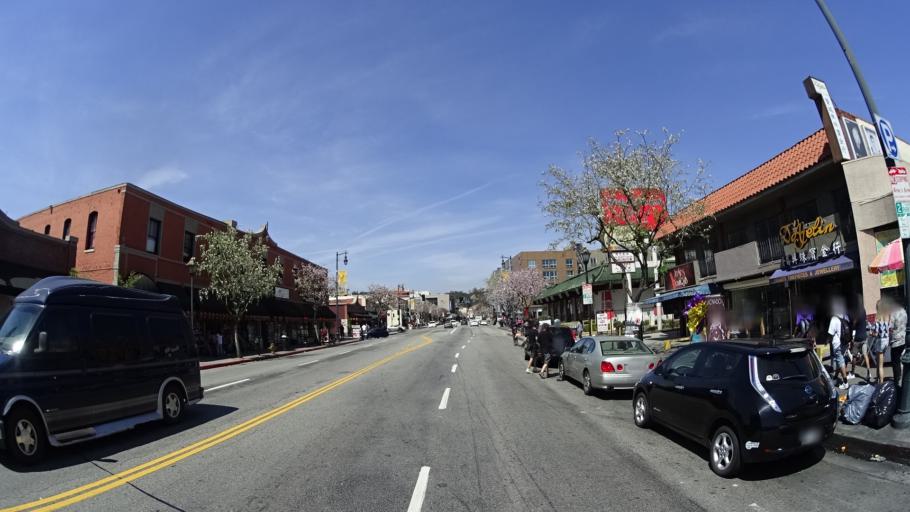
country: US
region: California
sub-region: Los Angeles County
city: Los Angeles
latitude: 34.0633
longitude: -118.2378
